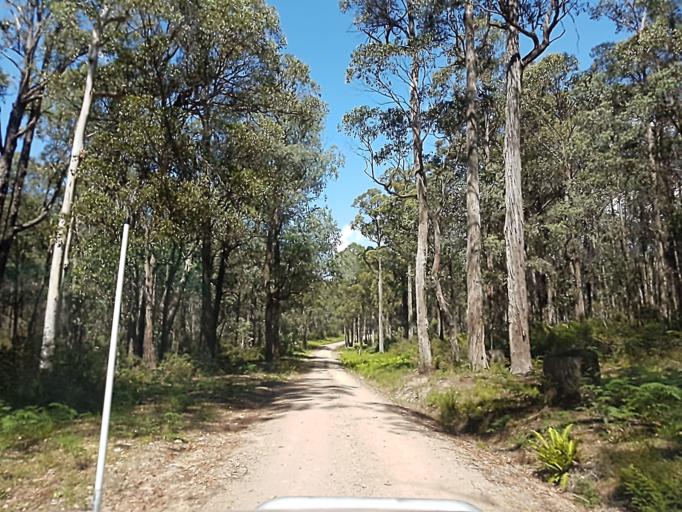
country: AU
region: Victoria
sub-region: East Gippsland
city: Lakes Entrance
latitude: -37.3021
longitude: 148.3248
